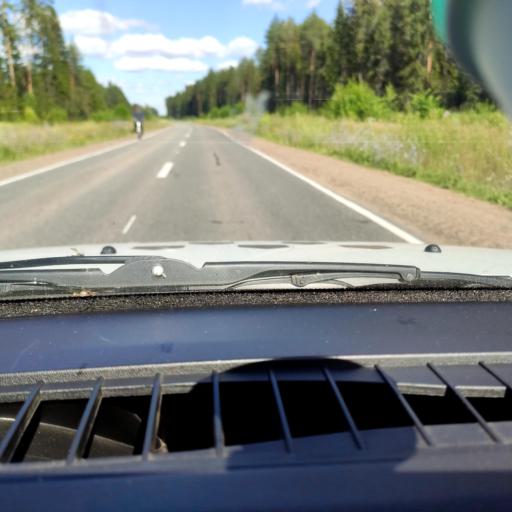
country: RU
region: Udmurtiya
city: Votkinsk
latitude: 57.0819
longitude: 54.0331
